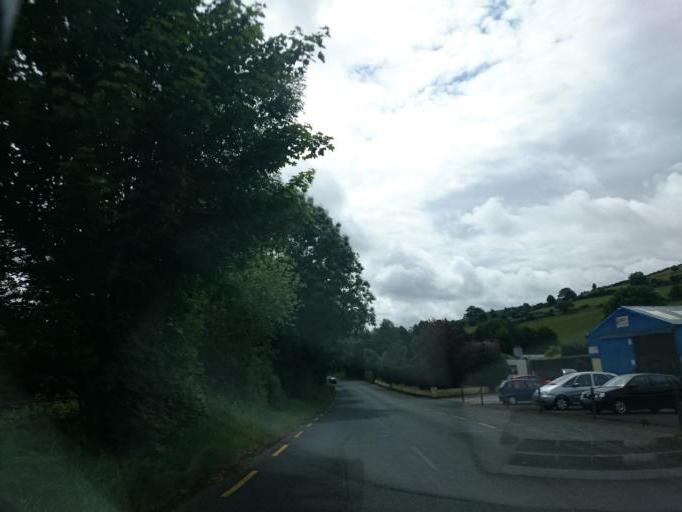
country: IE
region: Leinster
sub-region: Wicklow
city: Carnew
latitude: 52.8069
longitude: -6.4820
